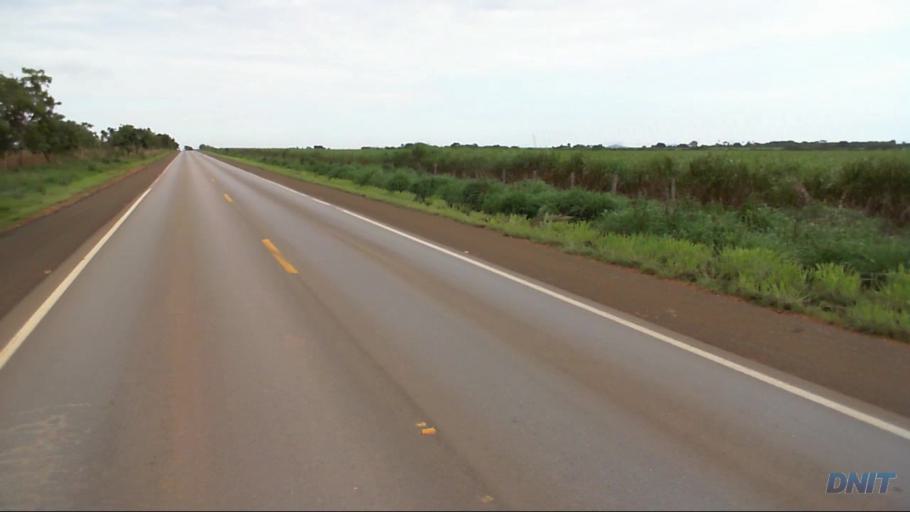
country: BR
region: Goias
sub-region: Uruacu
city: Uruacu
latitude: -14.7199
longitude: -49.1011
